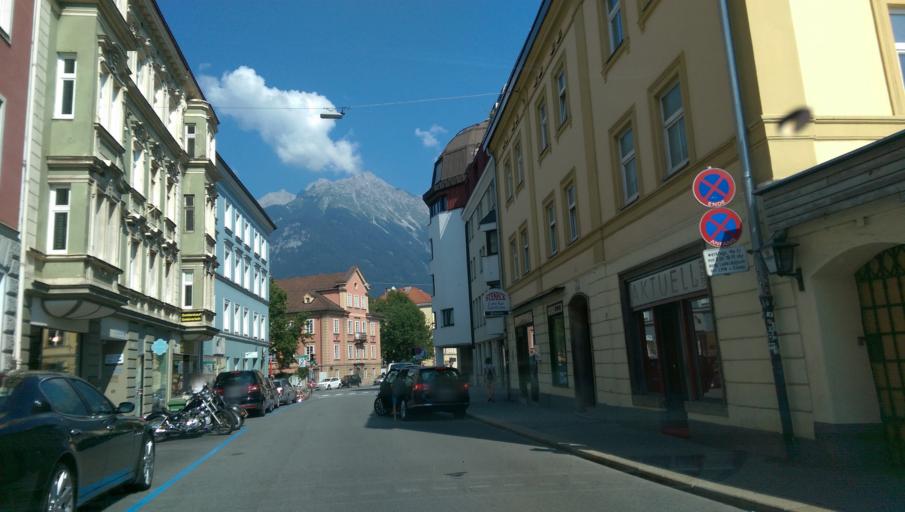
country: AT
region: Tyrol
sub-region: Innsbruck Stadt
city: Innsbruck
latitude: 47.2599
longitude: 11.3962
